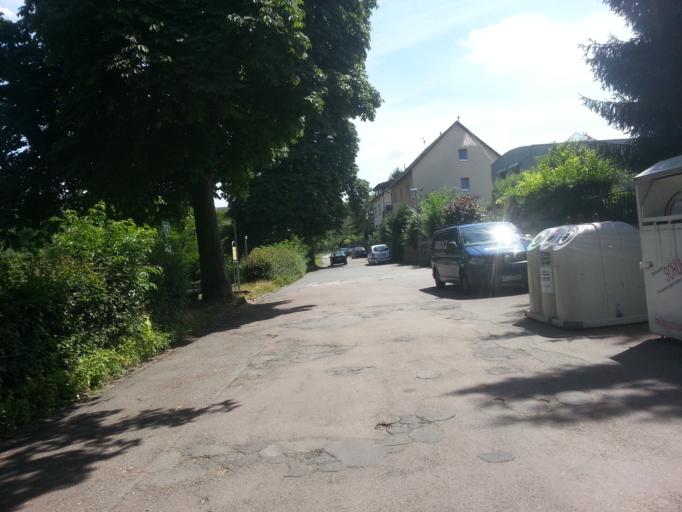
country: DE
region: Baden-Wuerttemberg
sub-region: Karlsruhe Region
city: Eppelheim
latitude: 49.4276
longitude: 8.6507
